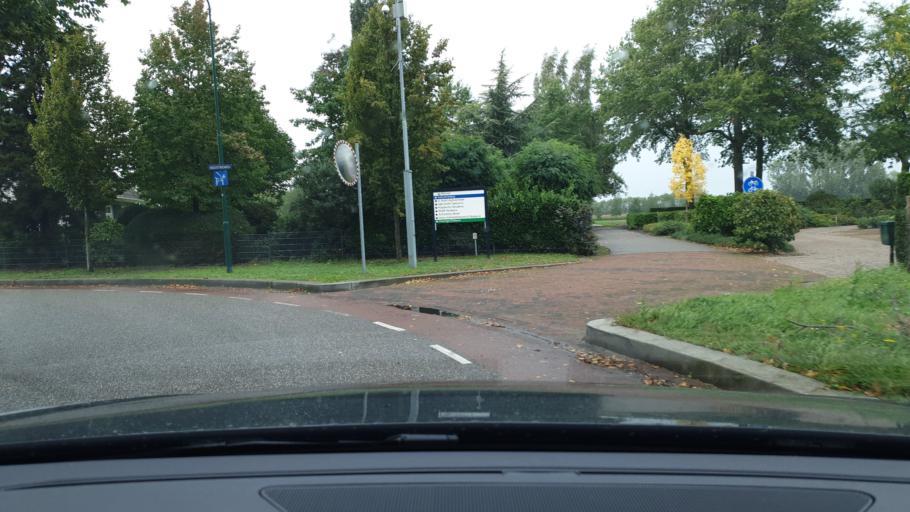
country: NL
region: North Brabant
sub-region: Gemeente Sint-Oedenrode
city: Sint-Oedenrode
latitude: 51.5560
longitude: 5.4848
